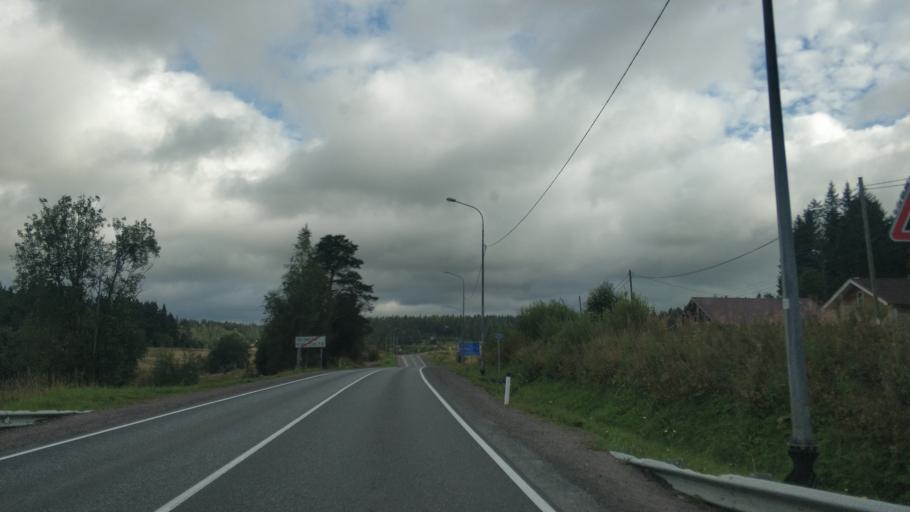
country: RU
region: Republic of Karelia
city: Khelyulya
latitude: 61.7563
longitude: 30.6567
